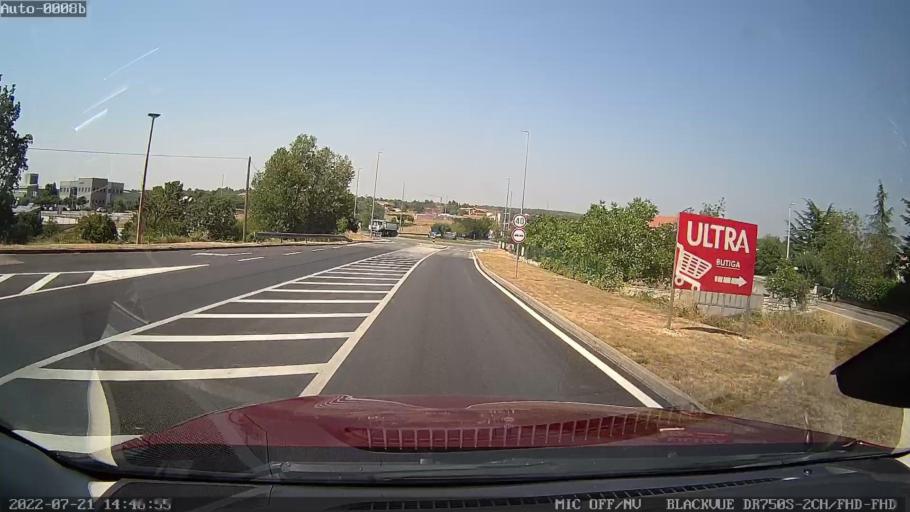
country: HR
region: Istarska
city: Pazin
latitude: 45.1405
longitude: 13.9012
